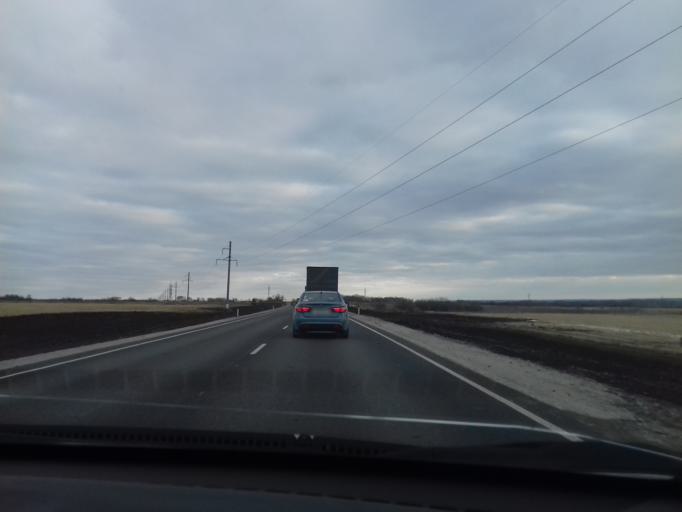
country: RU
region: Kurgan
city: Kataysk
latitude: 56.2948
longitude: 62.6654
